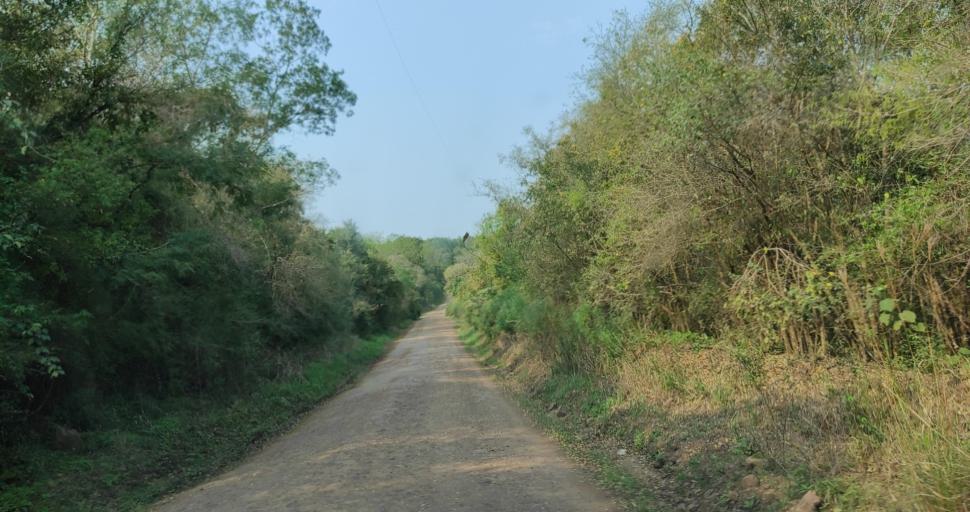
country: AR
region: Misiones
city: Cerro Azul
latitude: -27.6262
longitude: -55.5394
